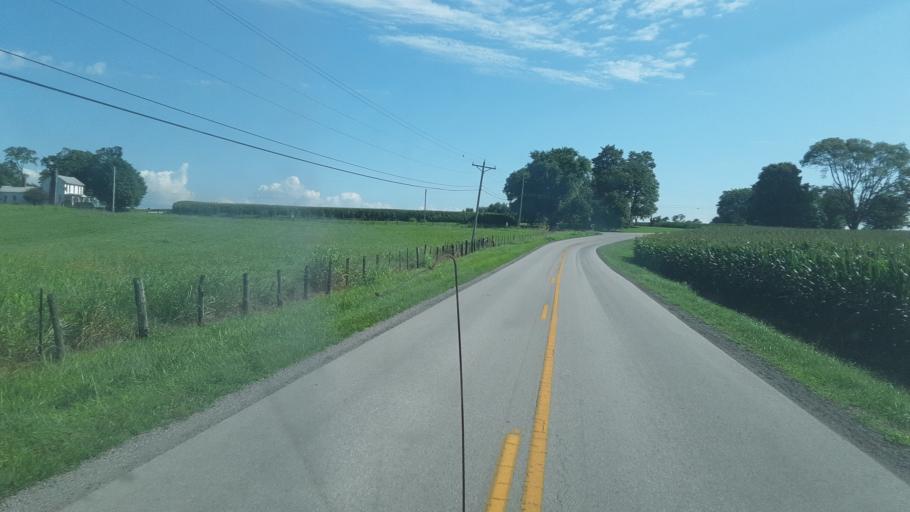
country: US
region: Kentucky
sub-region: Todd County
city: Guthrie
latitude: 36.7329
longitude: -87.2575
